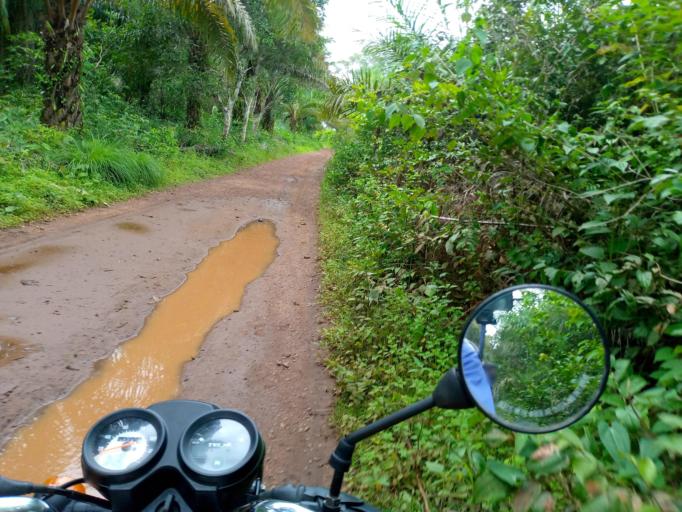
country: SL
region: Northern Province
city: Mange
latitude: 8.9810
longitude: -12.7123
